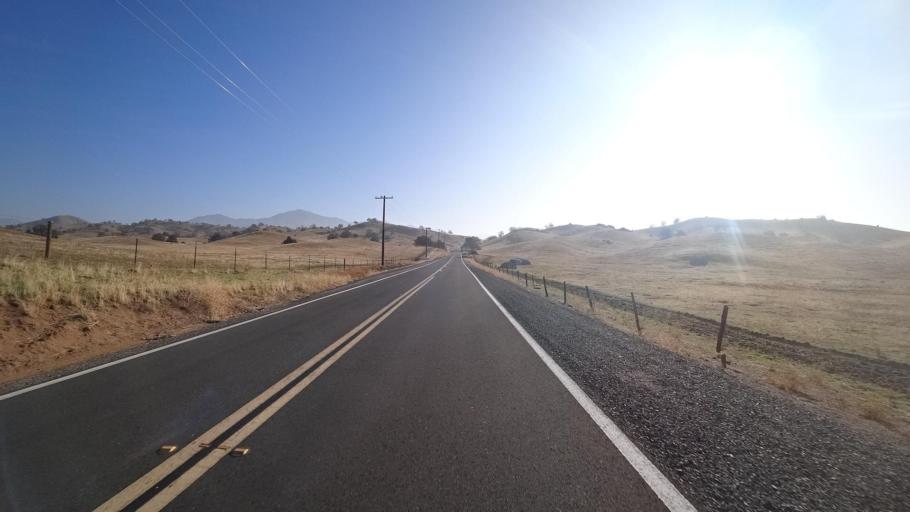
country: US
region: California
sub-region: Tulare County
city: Richgrove
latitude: 35.7417
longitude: -118.8767
